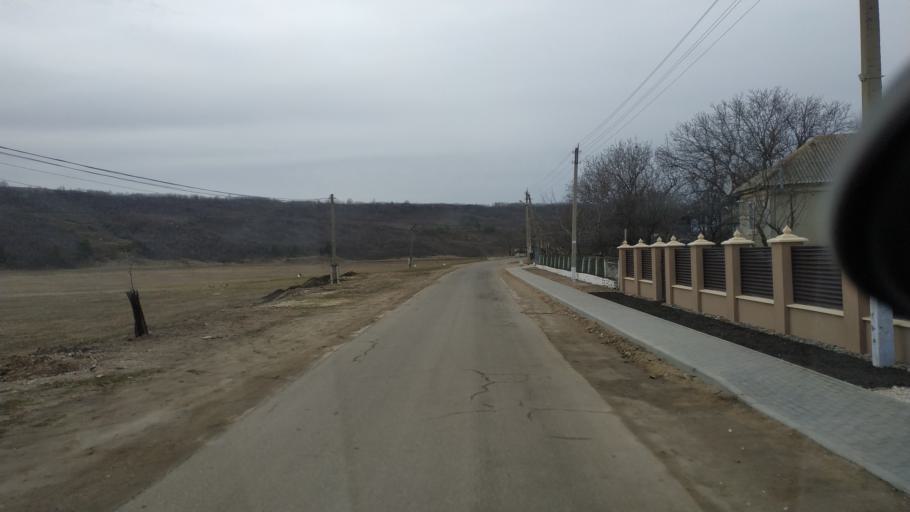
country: MD
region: Telenesti
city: Cocieri
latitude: 47.2650
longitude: 29.0483
